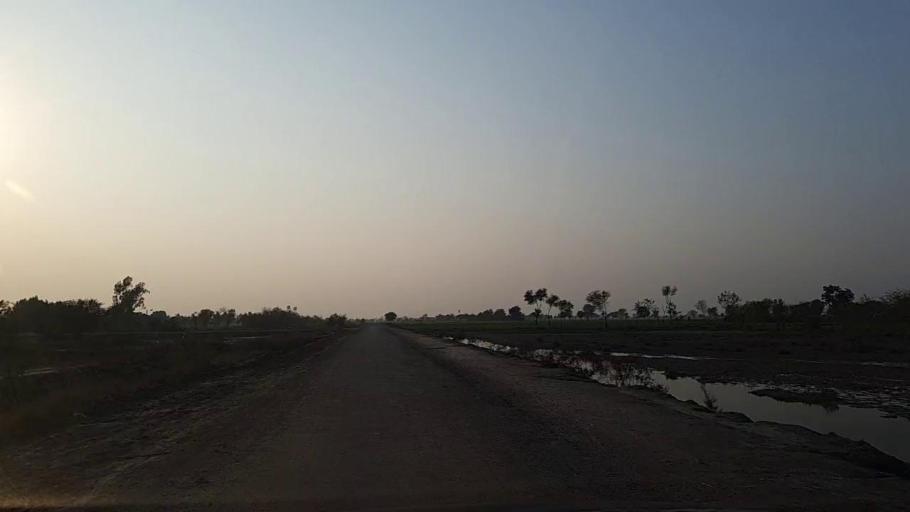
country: PK
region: Sindh
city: Daur
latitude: 26.4164
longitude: 68.3805
